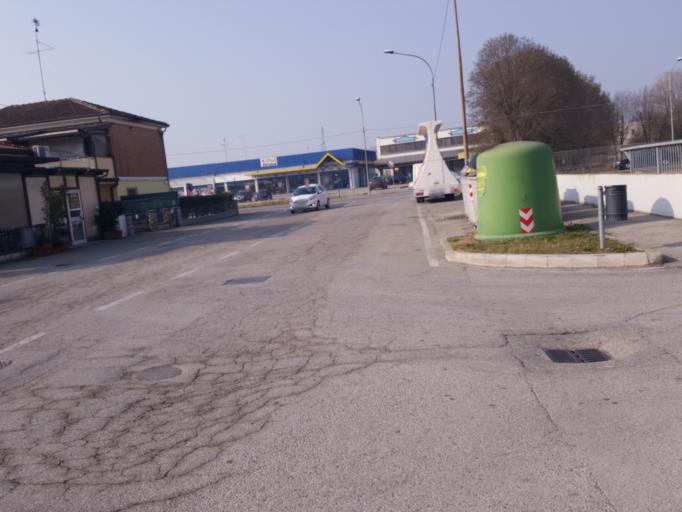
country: IT
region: Emilia-Romagna
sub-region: Provincia di Ferrara
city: Argenta
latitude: 44.6034
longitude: 11.8437
